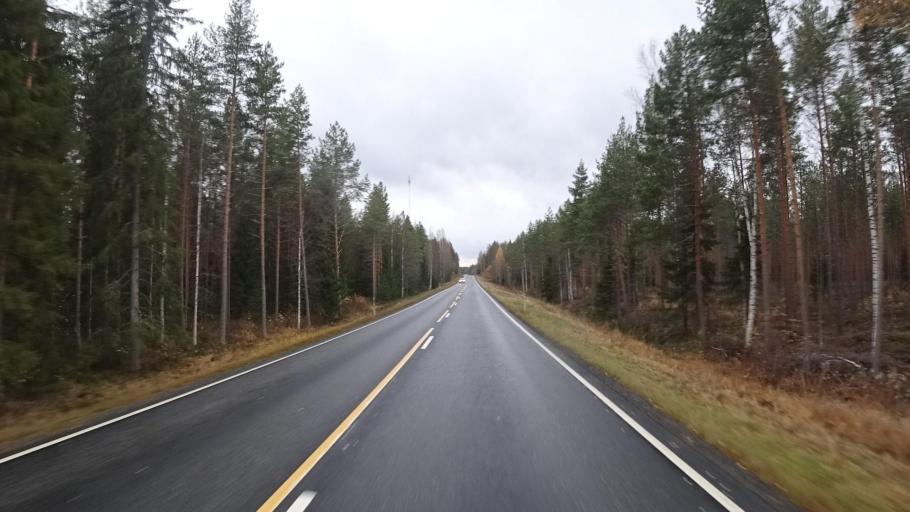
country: FI
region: Southern Savonia
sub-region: Mikkeli
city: Kangasniemi
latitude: 62.1534
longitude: 26.8171
